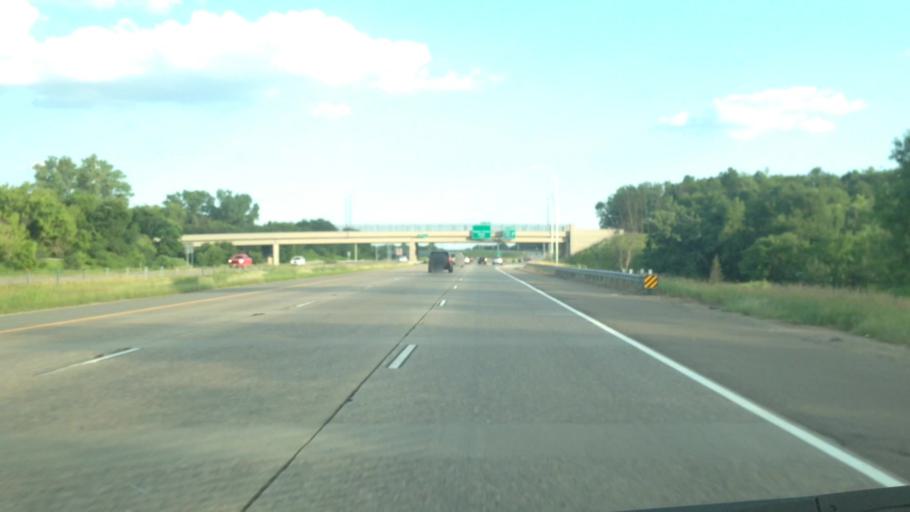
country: US
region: Minnesota
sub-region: Hennepin County
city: Rogers
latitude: 45.1465
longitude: -93.4998
